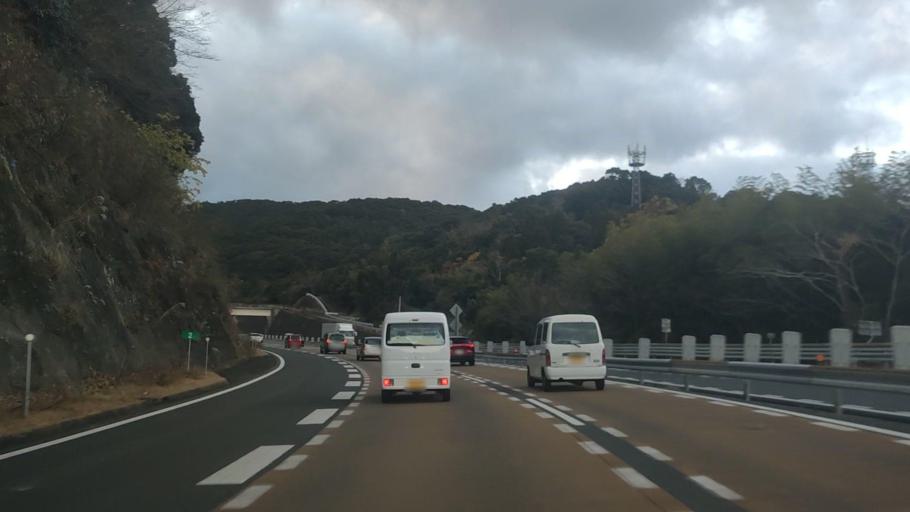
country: JP
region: Nagasaki
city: Obita
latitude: 32.8185
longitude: 129.9537
